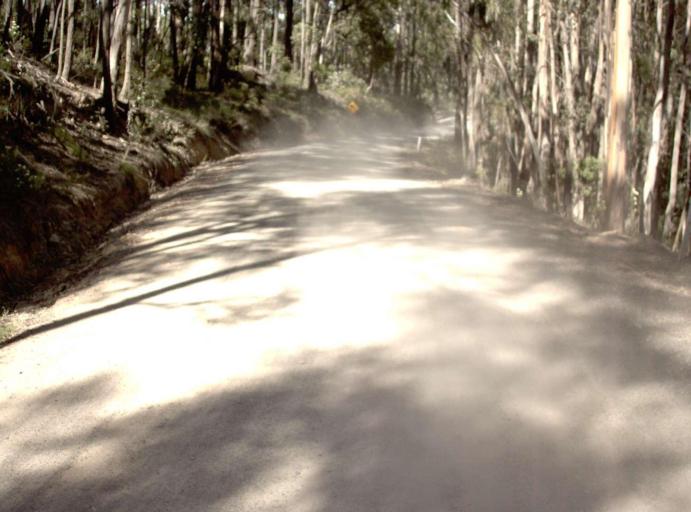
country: AU
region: New South Wales
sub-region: Bombala
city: Bombala
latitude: -37.2600
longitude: 148.7300
